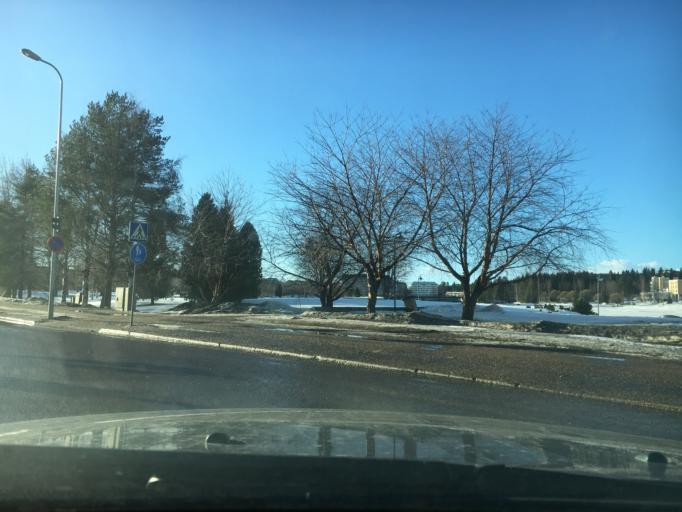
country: FI
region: Kainuu
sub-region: Kajaani
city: Kajaani
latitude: 64.2216
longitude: 27.7439
